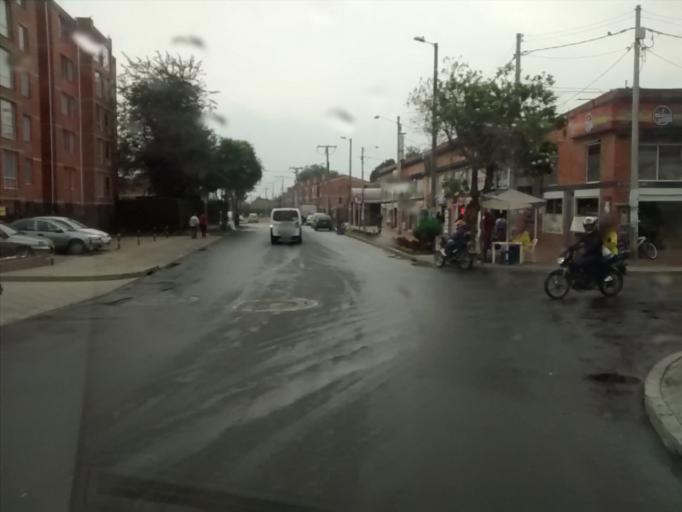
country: CO
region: Cundinamarca
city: Cota
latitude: 4.7575
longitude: -74.1019
